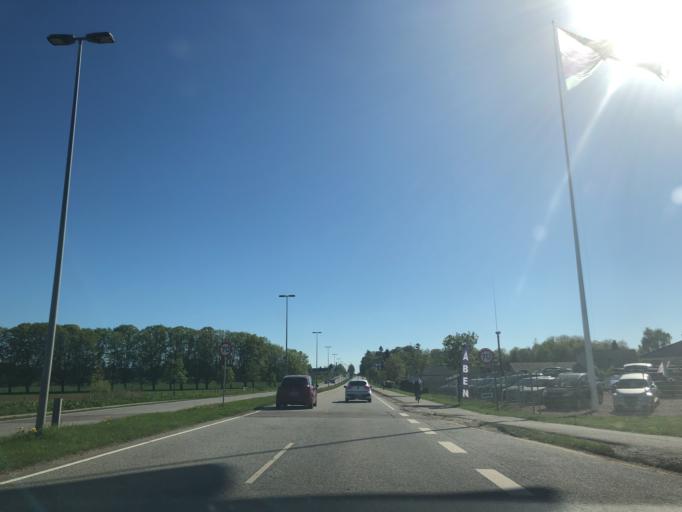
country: DK
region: Zealand
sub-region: Koge Kommune
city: Koge
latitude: 55.4260
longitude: 12.1507
